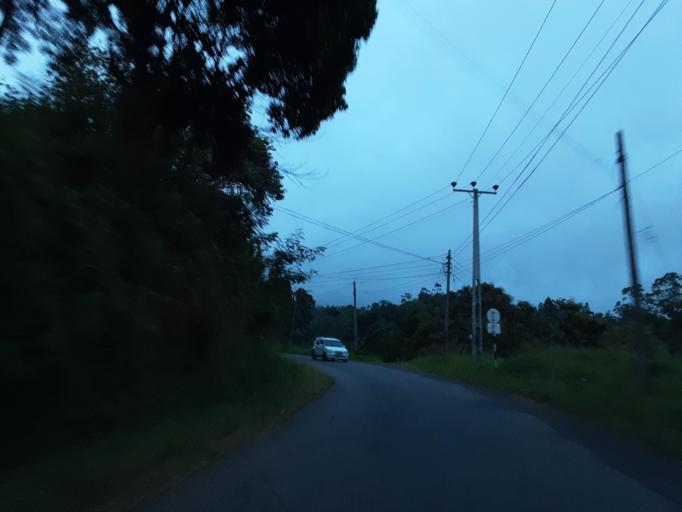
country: LK
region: Uva
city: Haputale
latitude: 6.9087
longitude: 80.9231
